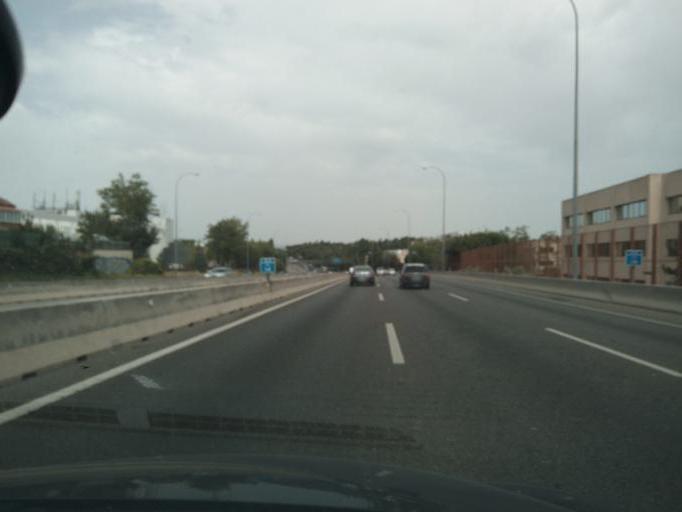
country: ES
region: Madrid
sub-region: Provincia de Madrid
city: Pozuelo de Alarcon
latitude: 40.4732
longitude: -3.8261
